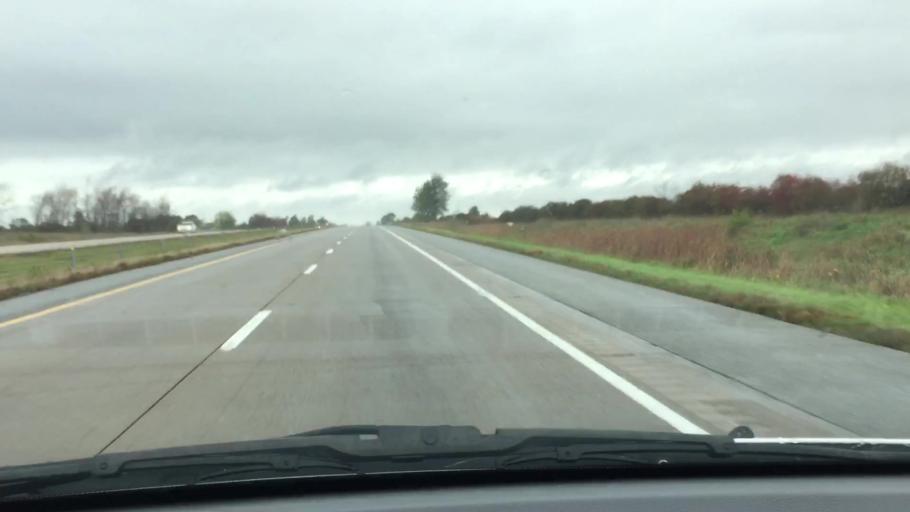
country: US
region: Iowa
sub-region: Poweshiek County
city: Brooklyn
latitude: 41.6963
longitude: -92.4126
